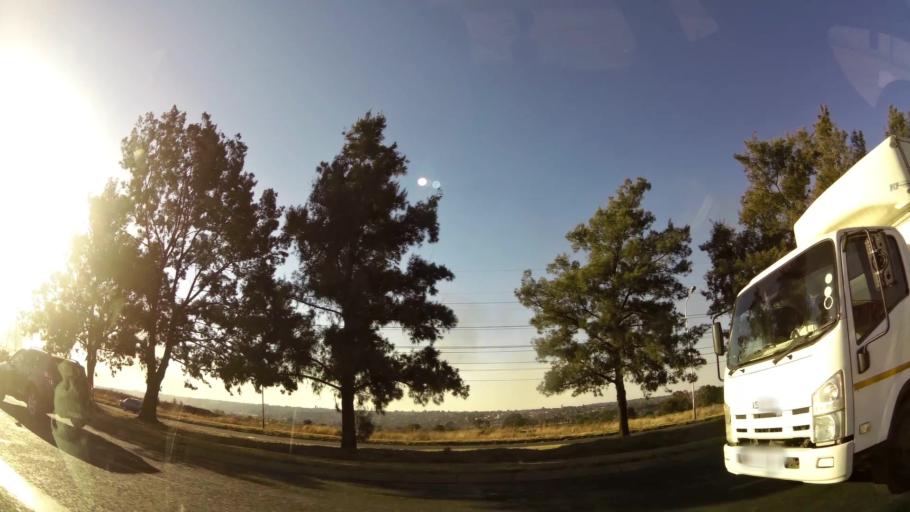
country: ZA
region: Gauteng
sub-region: City of Johannesburg Metropolitan Municipality
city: Roodepoort
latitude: -26.1813
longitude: 27.8889
